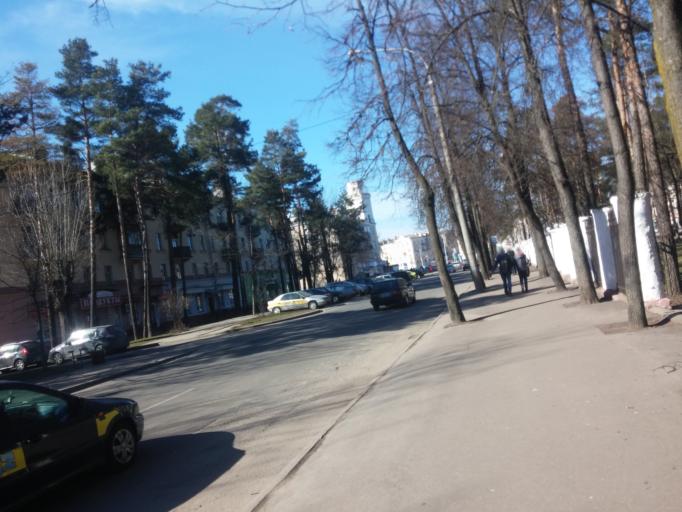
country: BY
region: Minsk
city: Vyaliki Trastsyanets
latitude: 53.8666
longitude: 27.6511
